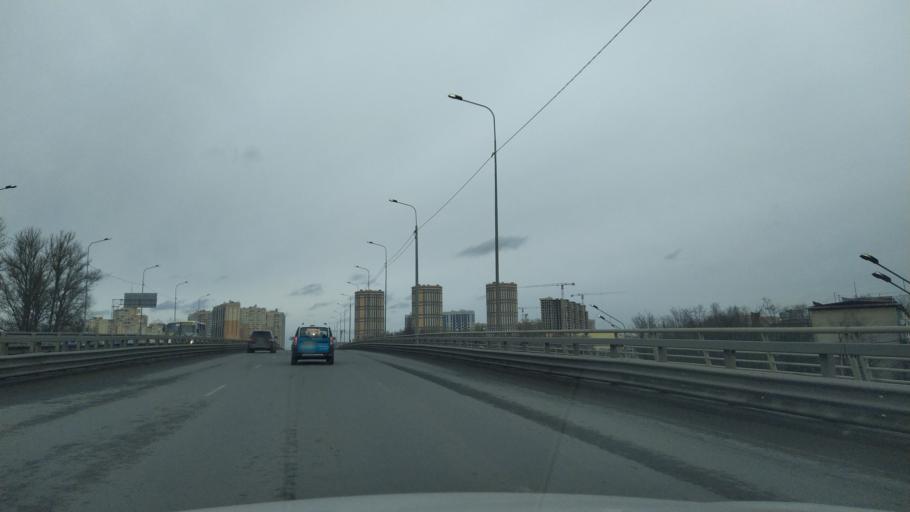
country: RU
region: Leningrad
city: Chernaya Rechka
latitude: 59.9915
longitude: 30.2988
